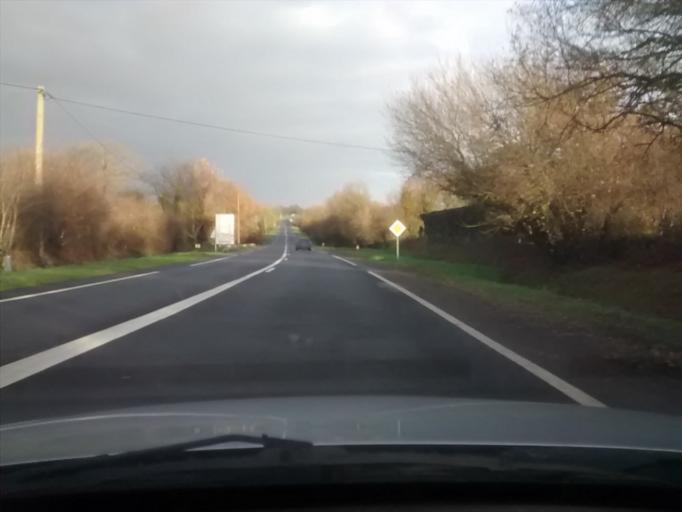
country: FR
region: Pays de la Loire
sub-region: Departement de la Mayenne
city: Loiron
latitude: 48.0708
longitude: -0.9272
